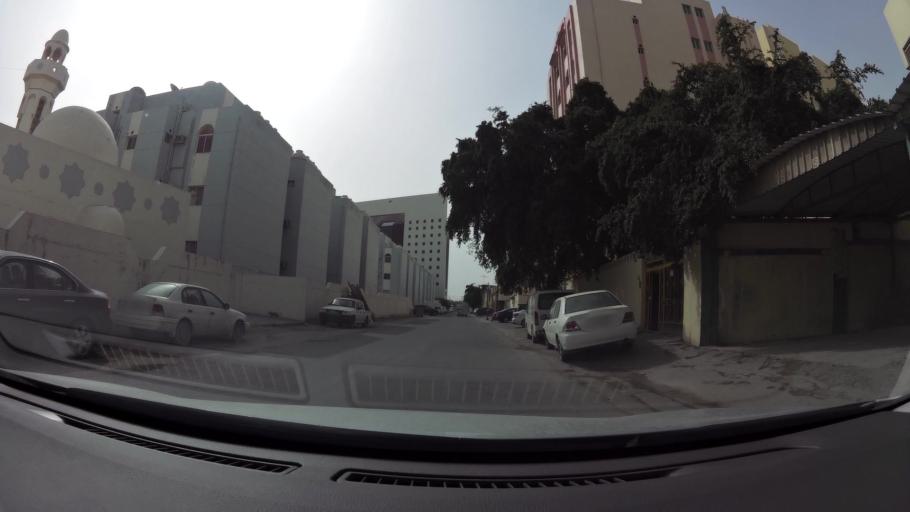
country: QA
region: Baladiyat ad Dawhah
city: Doha
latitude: 25.2761
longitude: 51.5502
